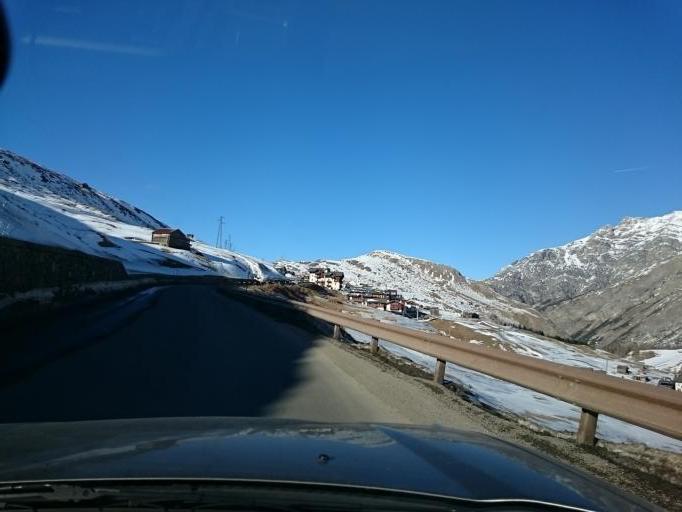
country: IT
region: Lombardy
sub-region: Provincia di Sondrio
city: Livigno
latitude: 46.5214
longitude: 10.1785
